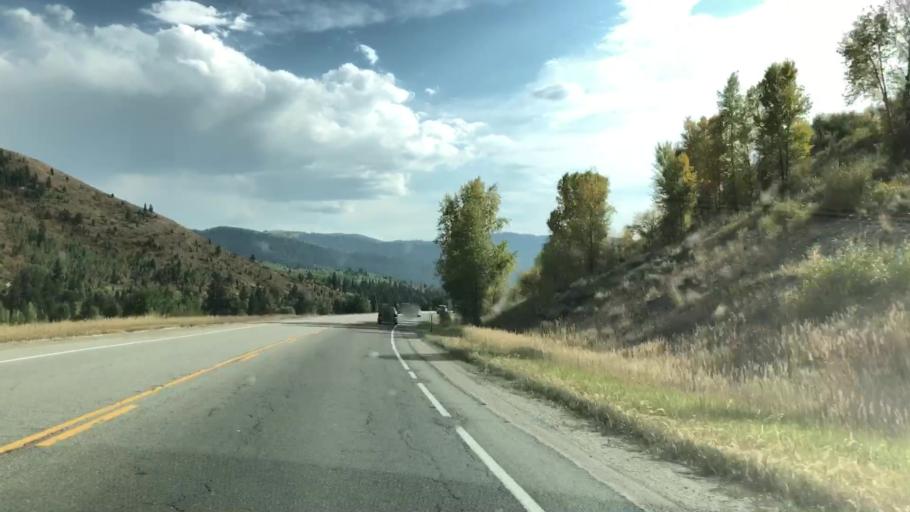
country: US
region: Wyoming
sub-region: Teton County
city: Hoback
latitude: 43.3517
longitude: -110.7201
